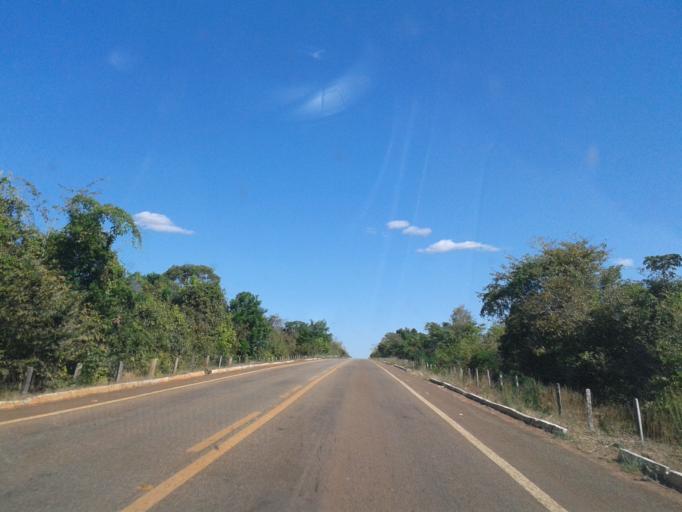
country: BR
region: Goias
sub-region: Crixas
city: Crixas
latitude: -14.0404
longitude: -50.3289
